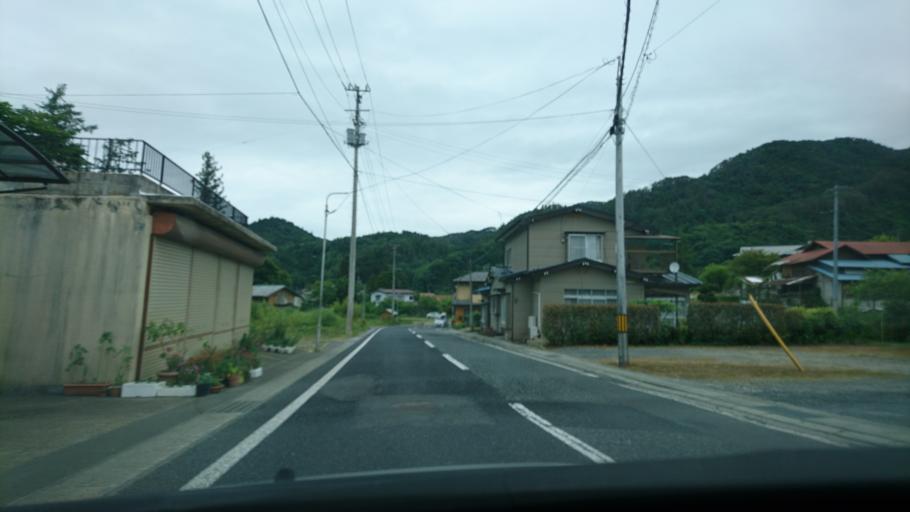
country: JP
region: Iwate
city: Ichinoseki
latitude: 38.9534
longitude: 141.2543
